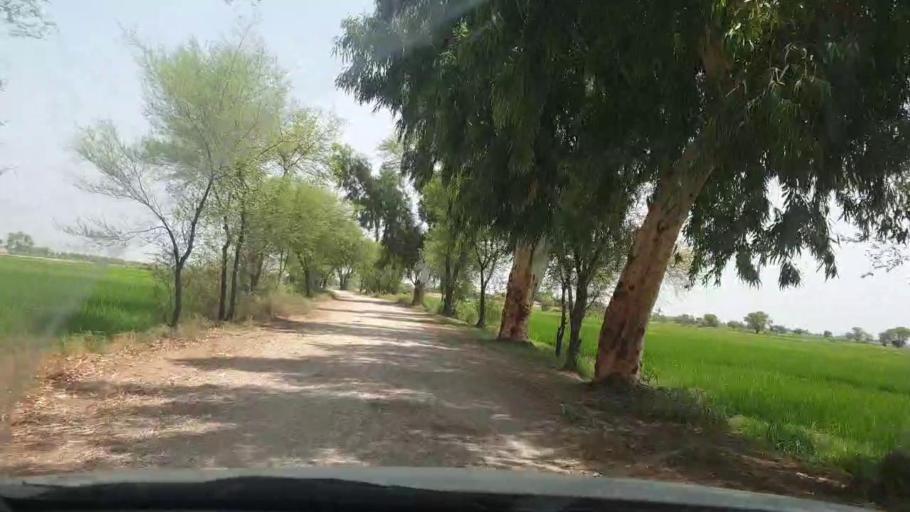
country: PK
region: Sindh
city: Lakhi
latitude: 27.8828
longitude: 68.7430
